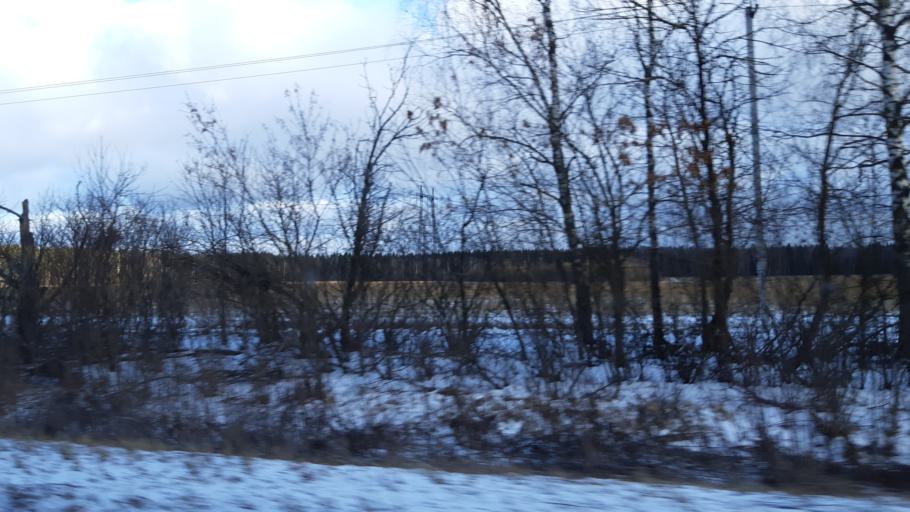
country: RU
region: Moskovskaya
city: Noginsk-9
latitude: 56.0417
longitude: 38.5528
